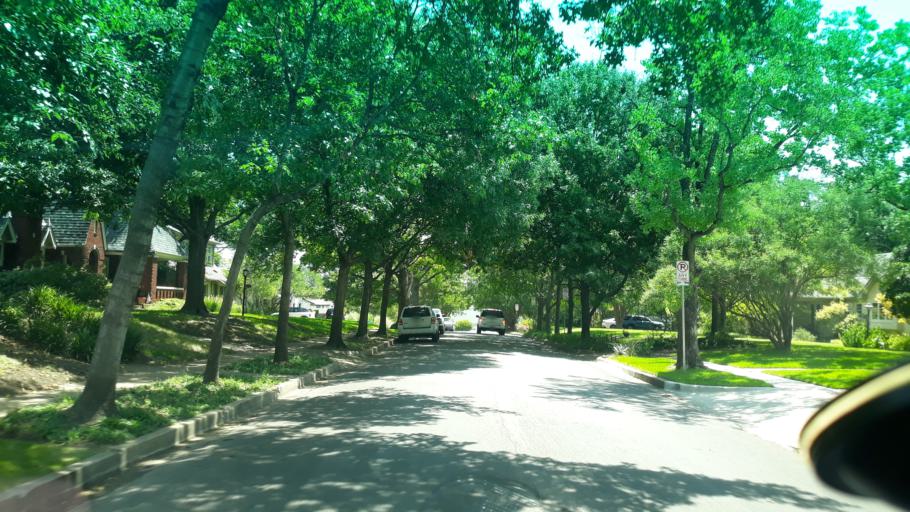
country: US
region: Texas
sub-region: Dallas County
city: Highland Park
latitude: 32.8135
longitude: -96.7366
